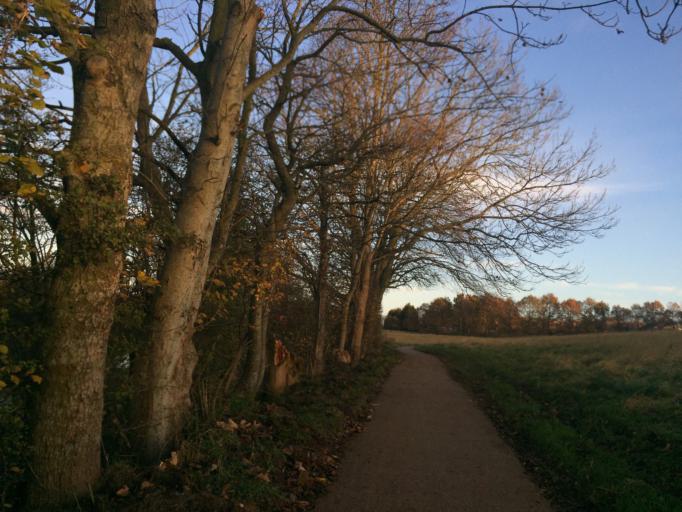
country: DK
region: Zealand
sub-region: Ringsted Kommune
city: Ringsted
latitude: 55.4227
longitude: 11.7756
